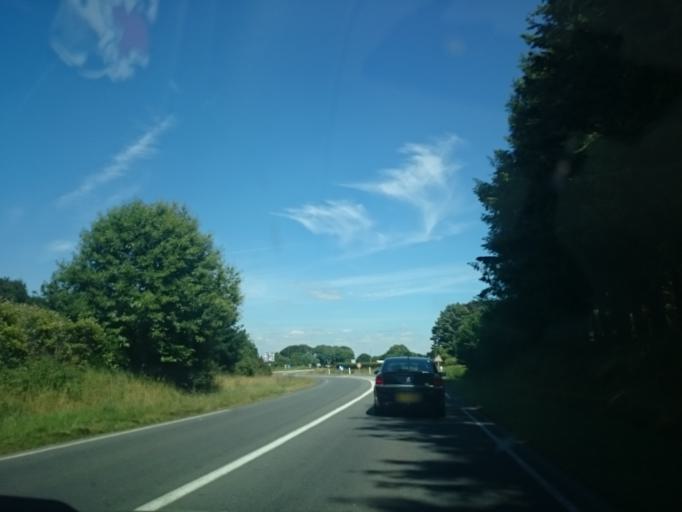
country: FR
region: Brittany
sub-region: Departement des Cotes-d'Armor
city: Rostrenen
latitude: 48.2425
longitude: -3.2996
